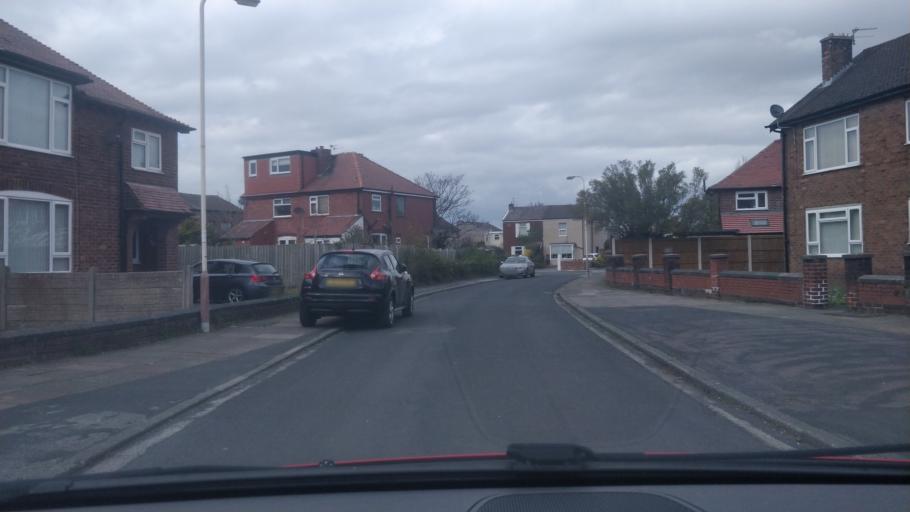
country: GB
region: England
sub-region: Sefton
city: Southport
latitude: 53.6200
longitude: -3.0123
